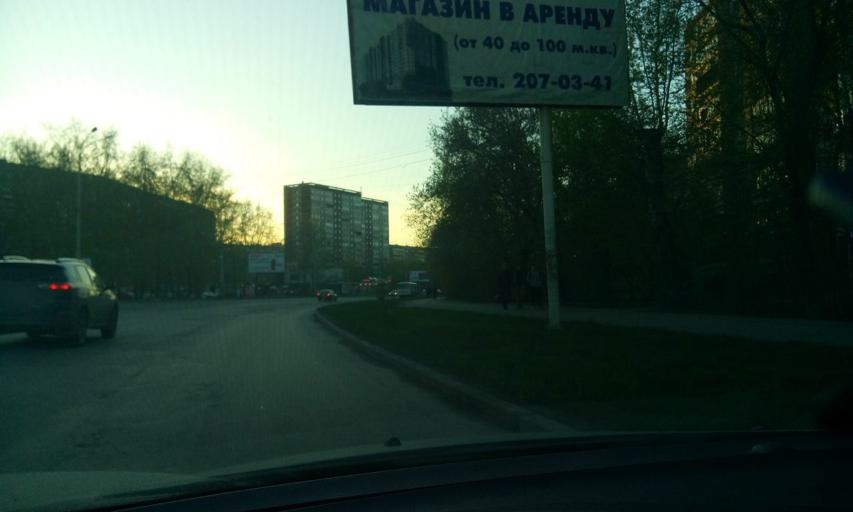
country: RU
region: Sverdlovsk
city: Yekaterinburg
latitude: 56.8359
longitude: 60.6818
